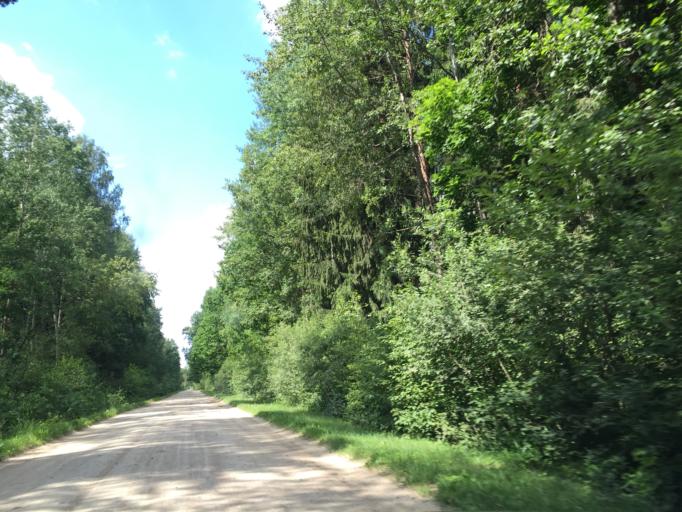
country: LV
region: Ozolnieku
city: Ozolnieki
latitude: 56.6868
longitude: 23.7569
